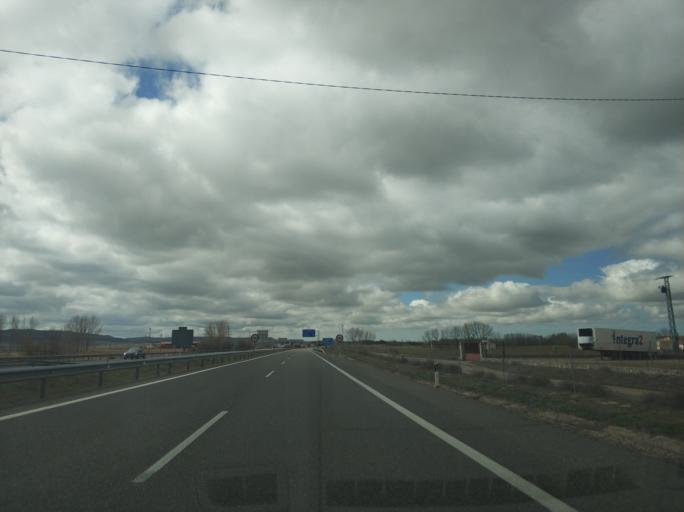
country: ES
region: Castille and Leon
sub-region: Provincia de Palencia
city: Quintana del Puente
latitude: 42.0740
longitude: -4.2141
